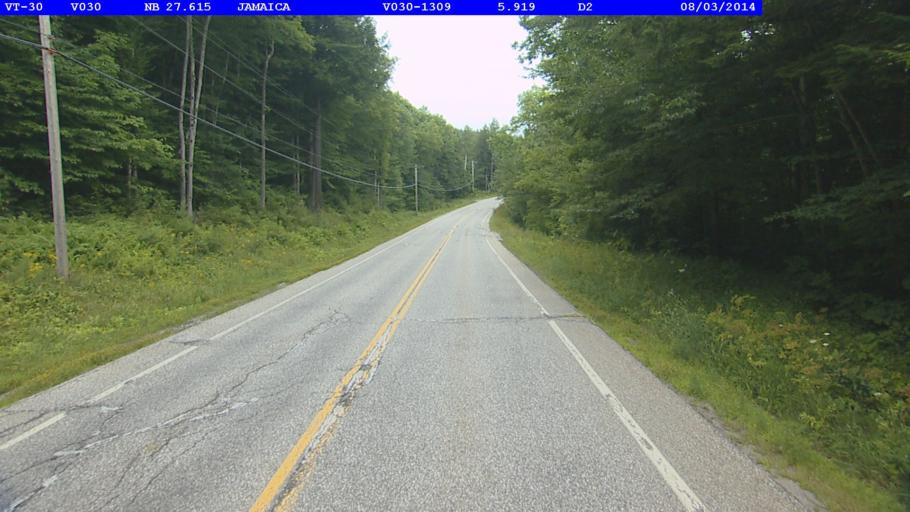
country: US
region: Vermont
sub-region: Windham County
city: Dover
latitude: 43.1175
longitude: -72.8049
